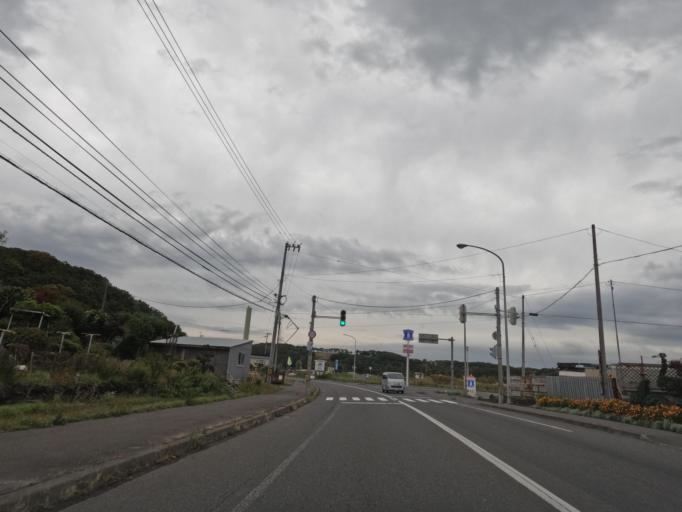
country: JP
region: Hokkaido
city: Date
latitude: 42.3852
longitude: 140.9100
